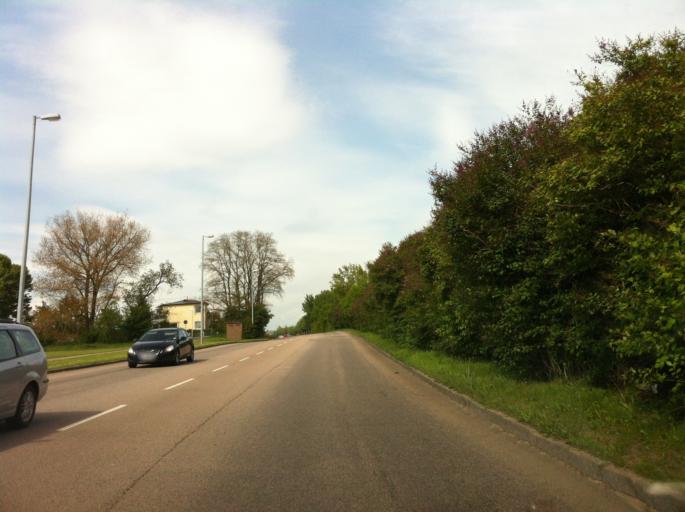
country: SE
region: Skane
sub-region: Landskrona
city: Landskrona
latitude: 55.8737
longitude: 12.8507
